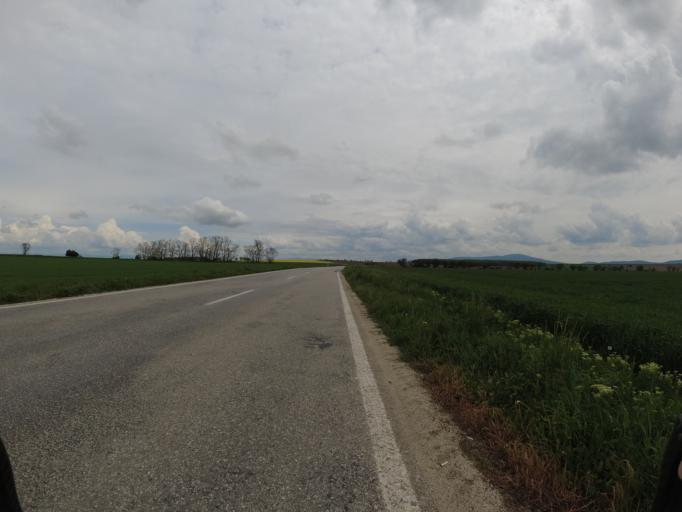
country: SK
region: Nitriansky
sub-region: Okres Nitra
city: Nitra
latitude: 48.5260
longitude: 18.0660
